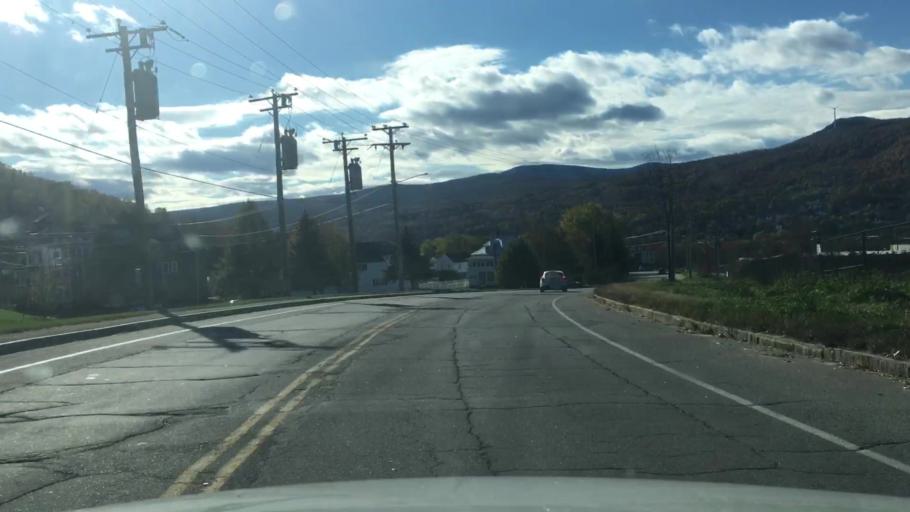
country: US
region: New Hampshire
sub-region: Coos County
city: Berlin
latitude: 44.4702
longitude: -71.1679
